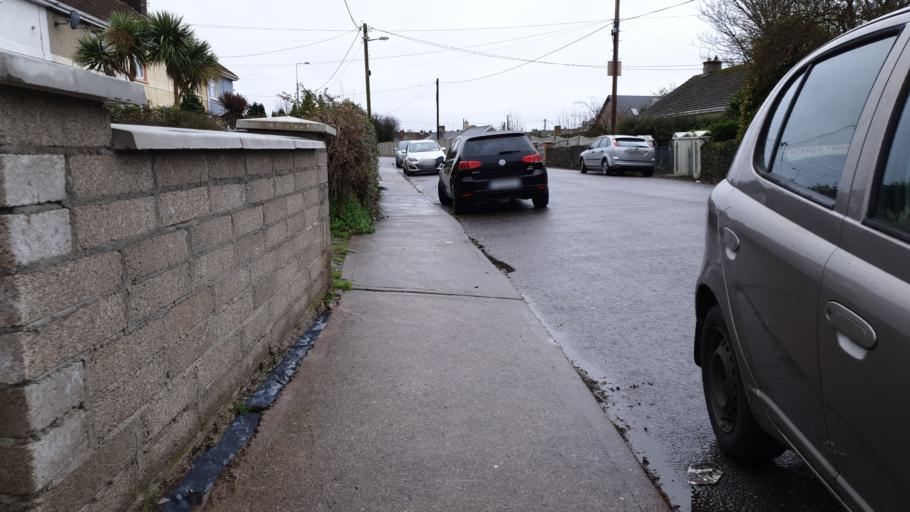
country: IE
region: Munster
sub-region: County Cork
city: Cork
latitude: 51.8970
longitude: -8.4082
